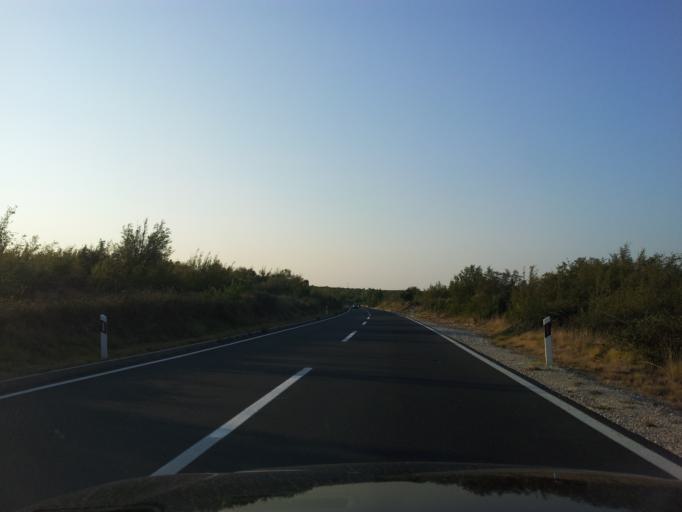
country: HR
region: Zadarska
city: Benkovac
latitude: 44.0134
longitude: 15.5706
